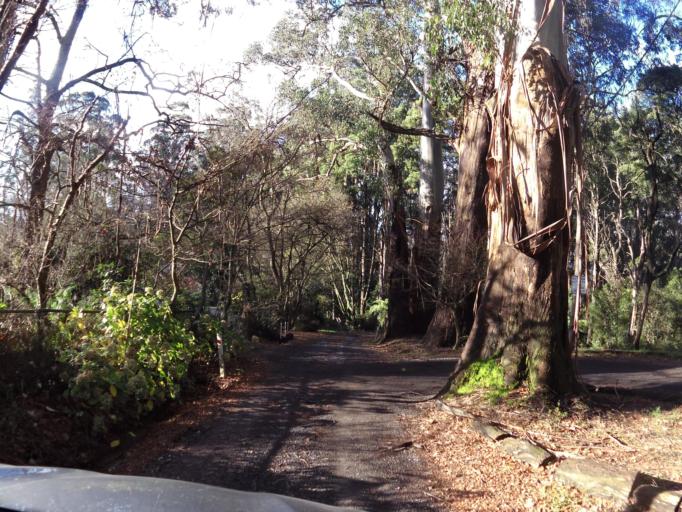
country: AU
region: Victoria
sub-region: Yarra Ranges
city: Kallista
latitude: -37.8850
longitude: 145.3623
